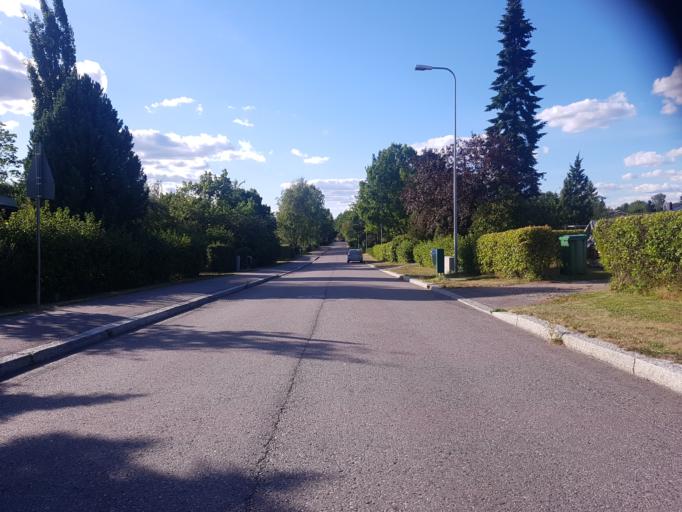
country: FI
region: Uusimaa
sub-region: Helsinki
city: Vantaa
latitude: 60.2829
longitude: 25.0061
